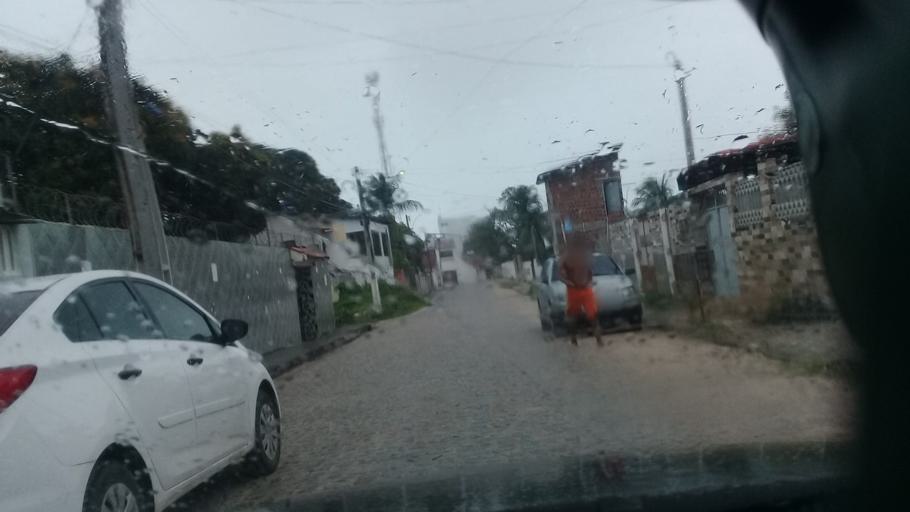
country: BR
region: Pernambuco
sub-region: Itamaraca
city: Itamaraca
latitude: -7.7434
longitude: -34.8268
